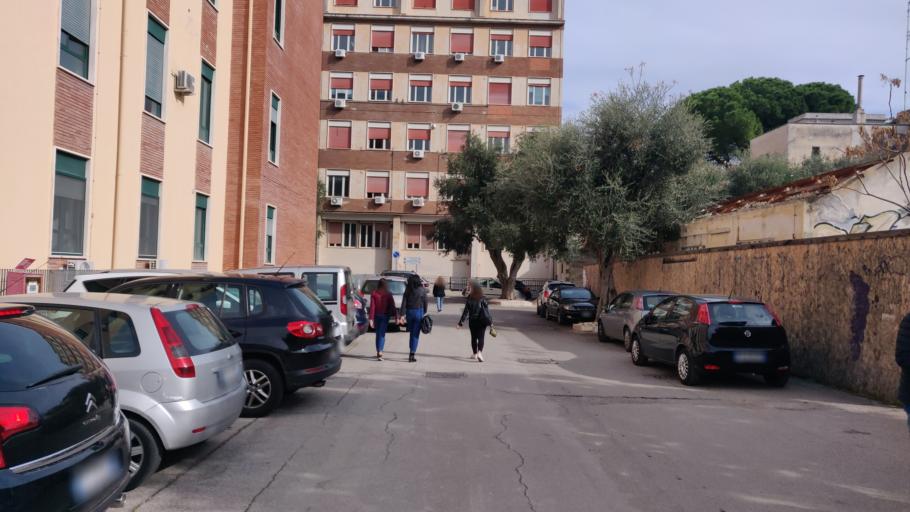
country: IT
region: Apulia
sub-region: Provincia di Bari
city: Bari
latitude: 41.1094
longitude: 16.8829
